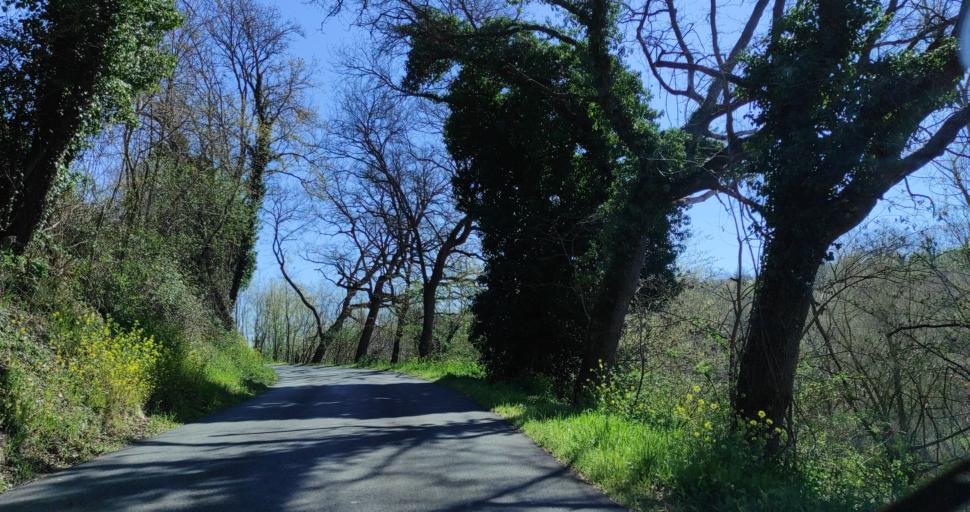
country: IT
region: The Marches
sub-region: Provincia di Macerata
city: Piediripa
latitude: 43.3124
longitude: 13.4865
